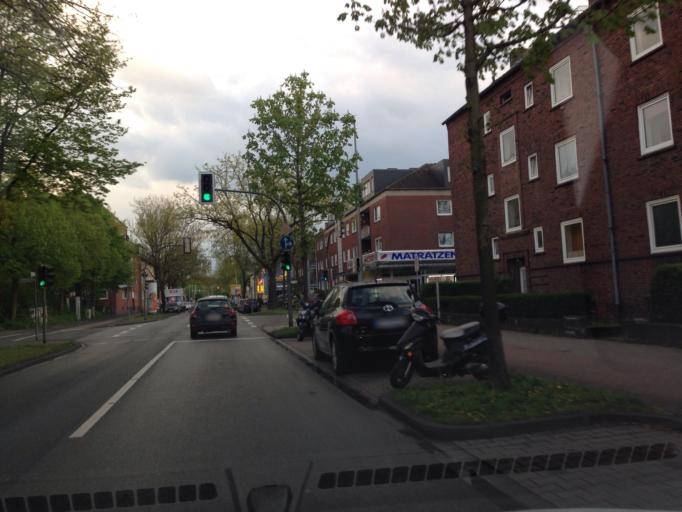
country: DE
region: North Rhine-Westphalia
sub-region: Regierungsbezirk Munster
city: Muenster
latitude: 51.9704
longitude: 7.6566
